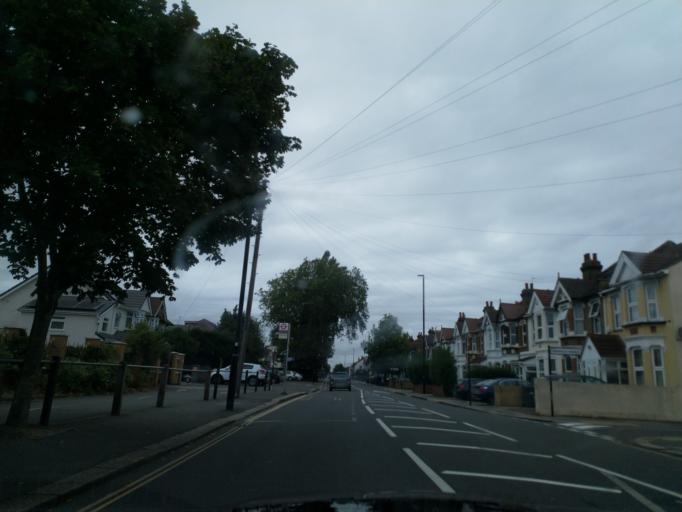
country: GB
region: England
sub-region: Greater London
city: Hounslow
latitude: 51.4593
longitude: -0.3742
